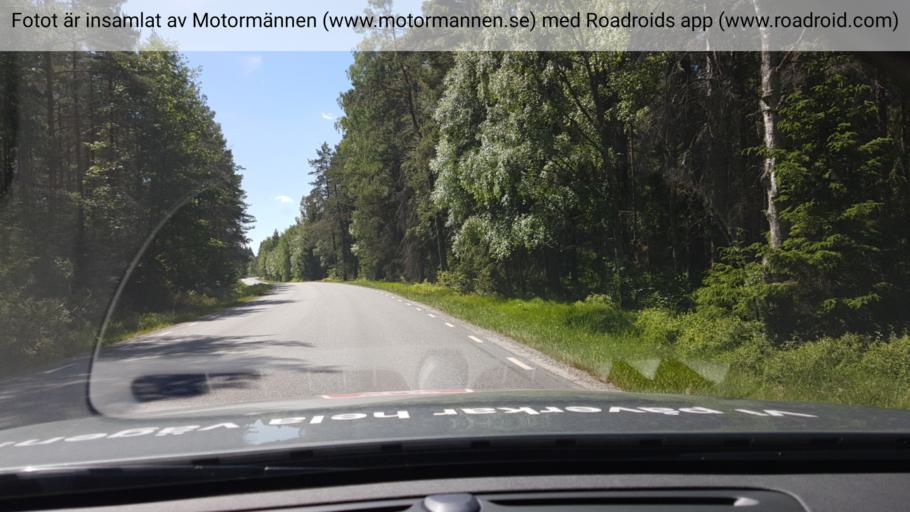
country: SE
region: Stockholm
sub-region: Haninge Kommun
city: Haninge
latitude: 59.1581
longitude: 18.1805
